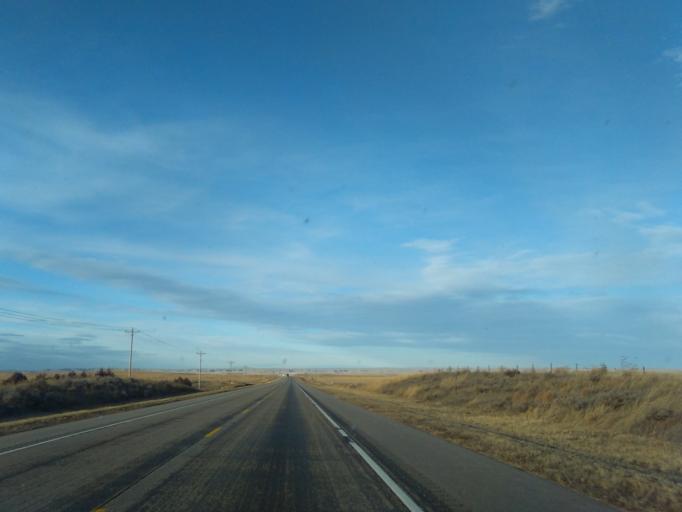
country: US
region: Nebraska
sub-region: Morrill County
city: Bridgeport
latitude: 41.5737
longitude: -102.9843
